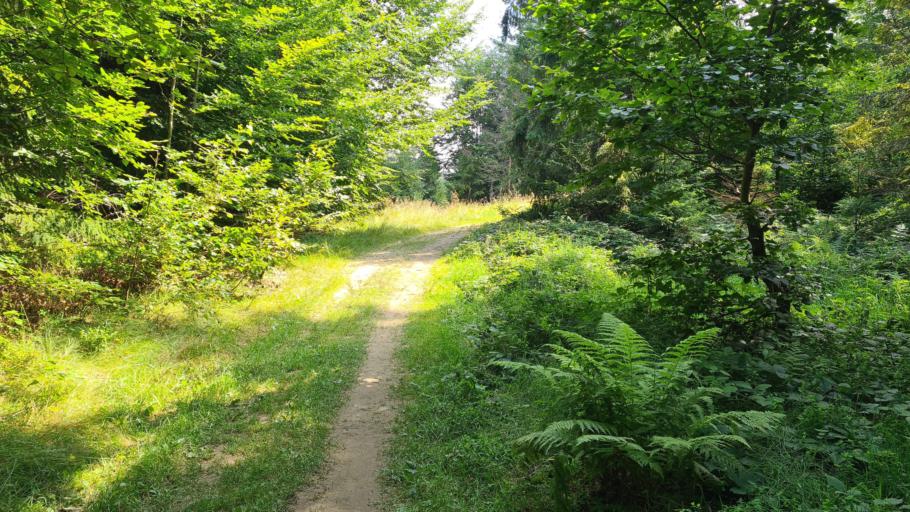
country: PL
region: Lesser Poland Voivodeship
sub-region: Powiat nowosadecki
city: Rytro
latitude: 49.4103
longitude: 20.6276
